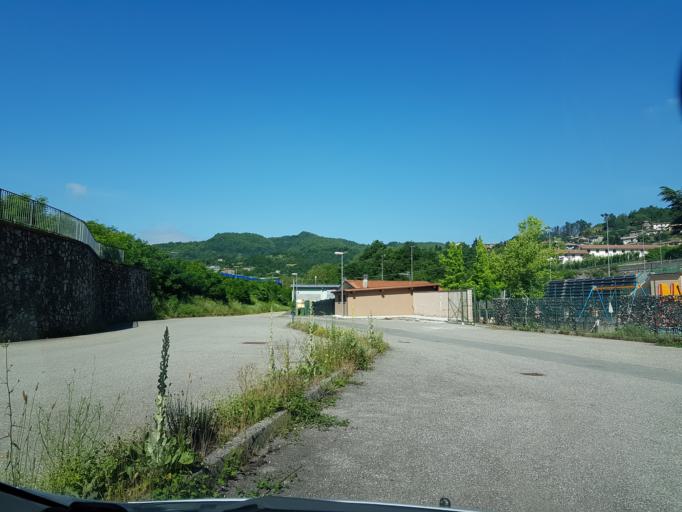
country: IT
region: Tuscany
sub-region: Provincia di Lucca
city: Piazza al Serchio-San Michele
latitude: 44.1833
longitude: 10.2957
